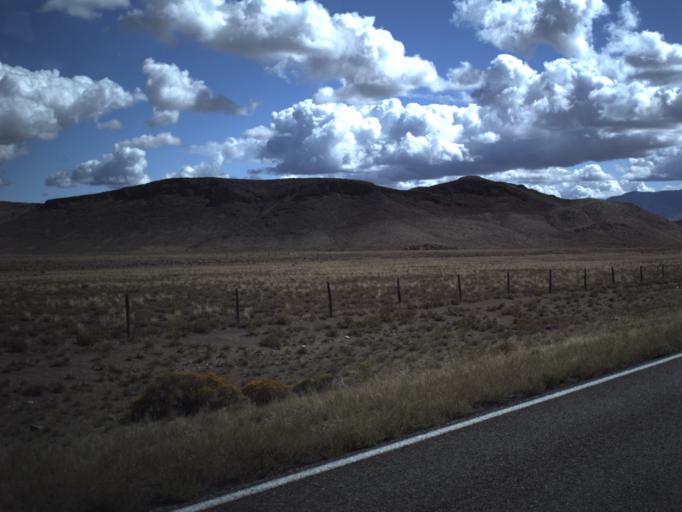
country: US
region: Utah
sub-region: Beaver County
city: Milford
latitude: 38.5977
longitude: -113.8278
